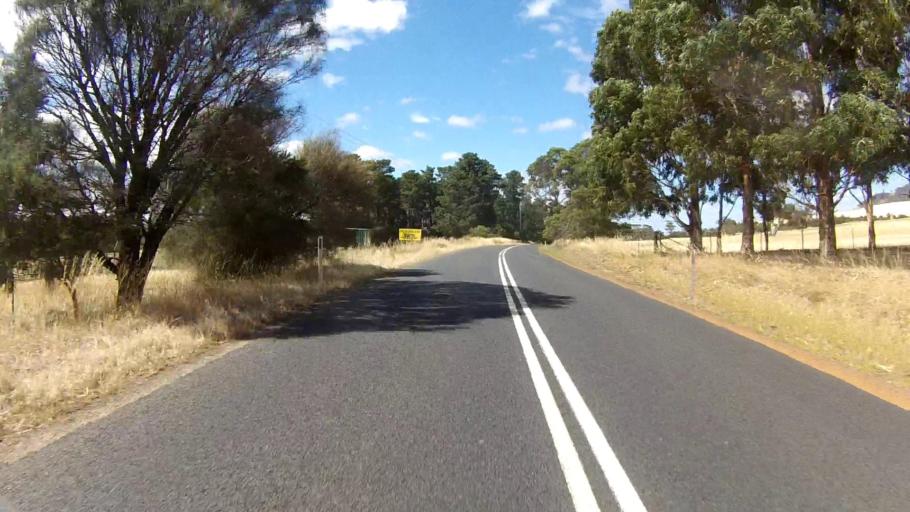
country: AU
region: Tasmania
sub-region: Sorell
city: Sorell
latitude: -42.6122
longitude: 147.4271
